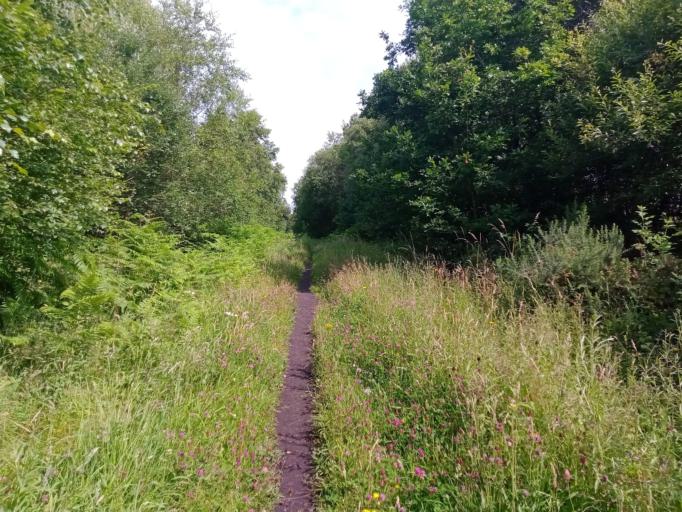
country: IE
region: Leinster
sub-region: Laois
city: Abbeyleix
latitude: 52.8890
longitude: -7.3503
